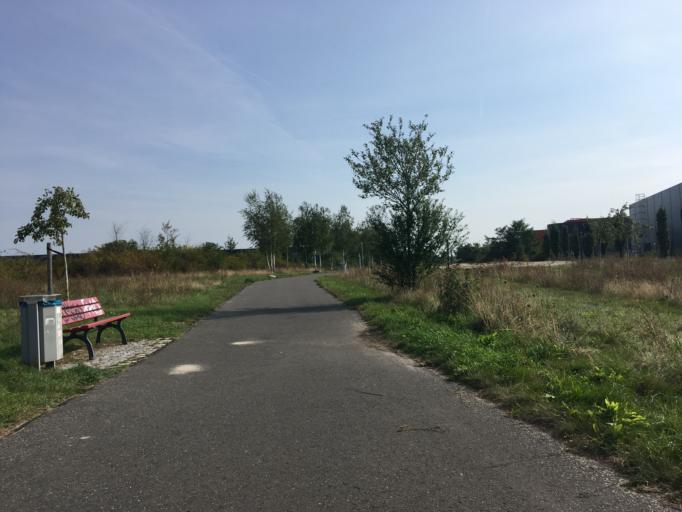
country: DE
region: Berlin
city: Altglienicke
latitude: 52.3909
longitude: 13.5387
